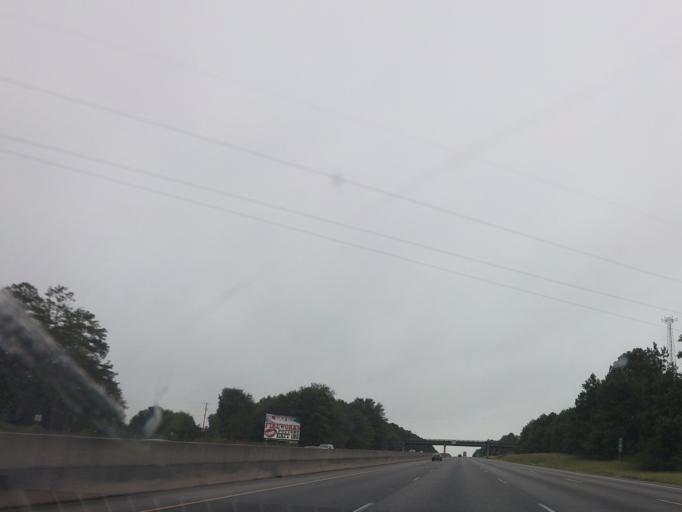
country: US
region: Georgia
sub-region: Monroe County
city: Forsyth
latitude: 33.0111
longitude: -83.8784
